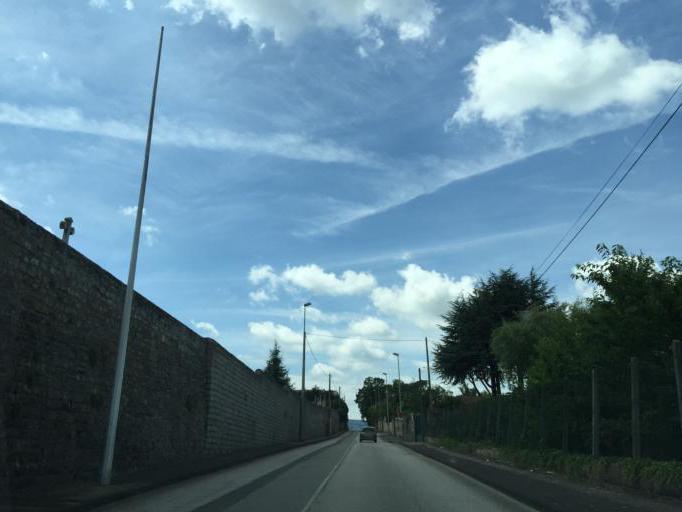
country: FR
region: Rhone-Alpes
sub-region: Departement de la Loire
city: Saint-Chamond
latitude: 45.4826
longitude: 4.5158
